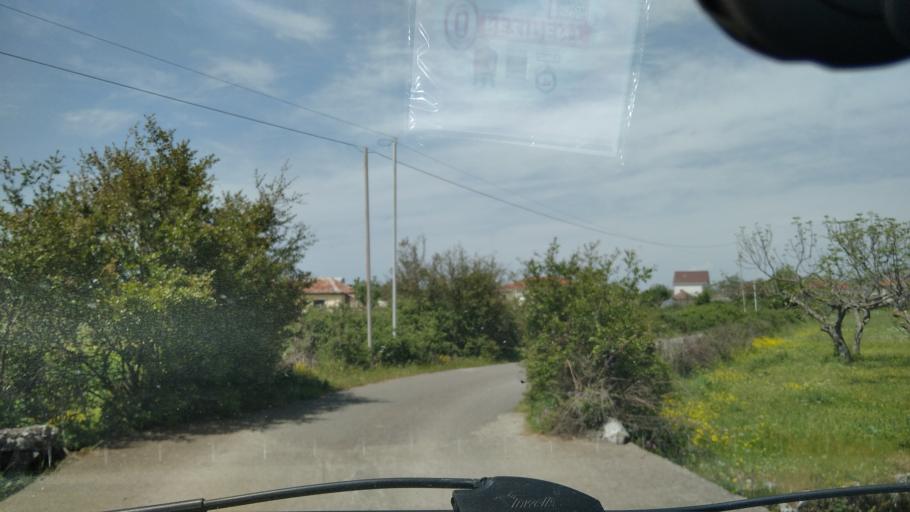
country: AL
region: Shkoder
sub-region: Rrethi i Malesia e Madhe
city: Gruemire
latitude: 42.1446
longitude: 19.5454
